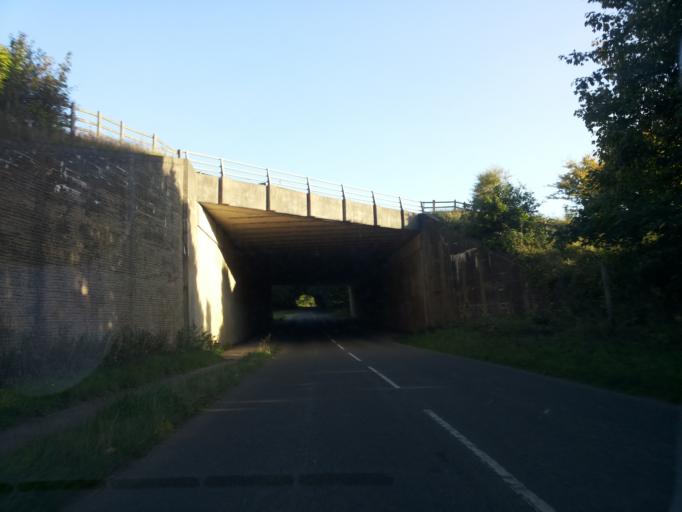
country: GB
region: England
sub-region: Derbyshire
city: Tibshelf
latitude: 53.1706
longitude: -1.3257
